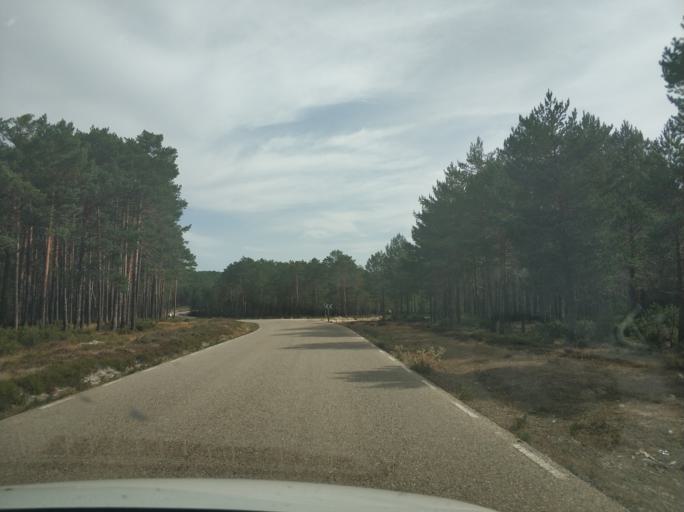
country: ES
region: Castille and Leon
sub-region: Provincia de Soria
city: Navaleno
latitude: 41.8546
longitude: -2.9738
